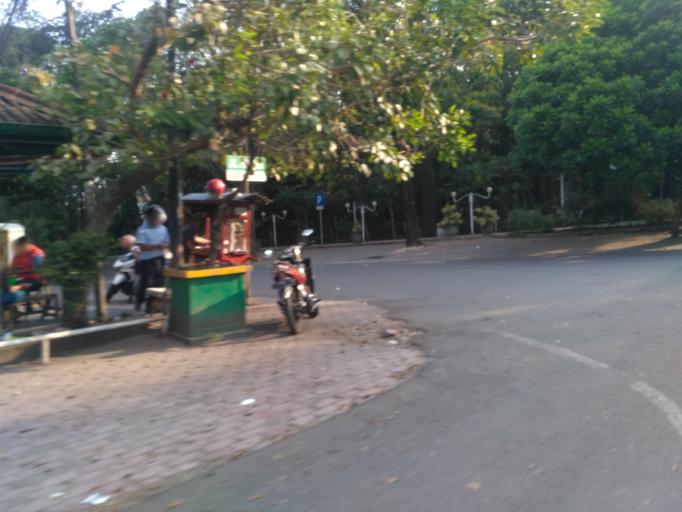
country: ID
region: East Java
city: Malang
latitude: -7.9685
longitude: 112.6280
